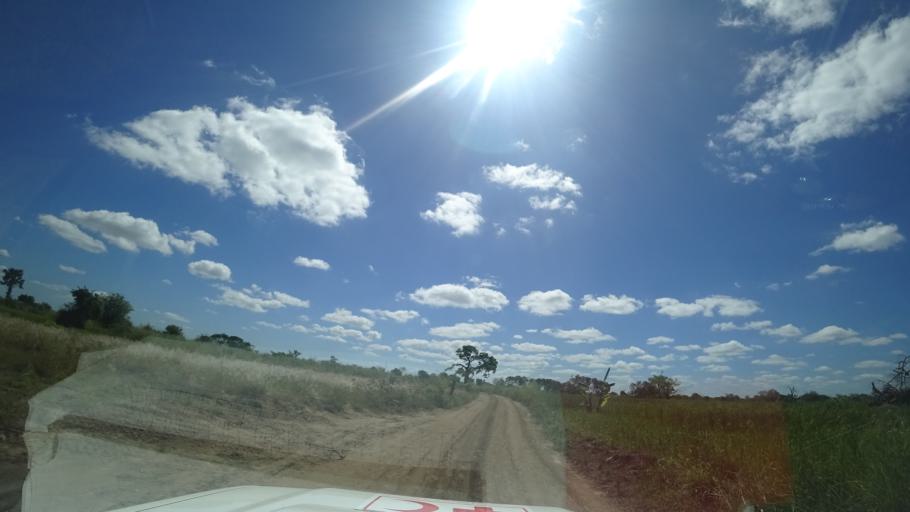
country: MZ
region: Sofala
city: Dondo
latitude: -19.4643
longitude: 34.5954
